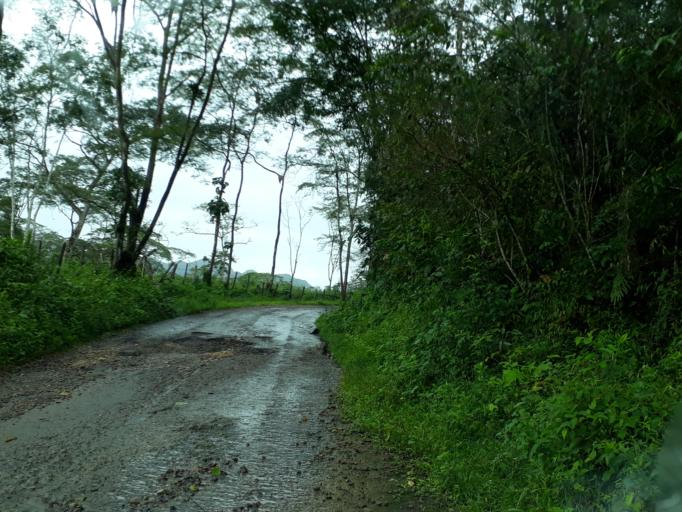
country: CO
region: Boyaca
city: Santa Maria
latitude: 4.6962
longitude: -73.3039
